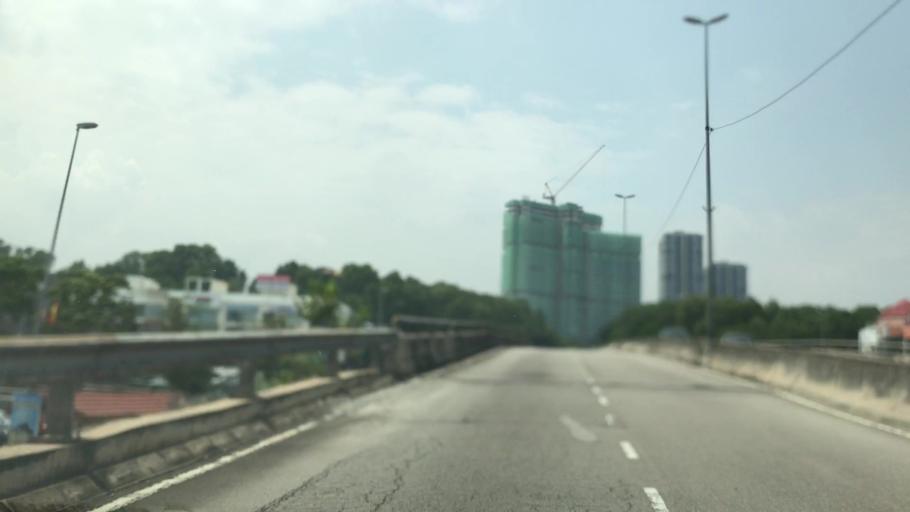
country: MY
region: Selangor
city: Subang Jaya
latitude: 3.0248
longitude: 101.6175
